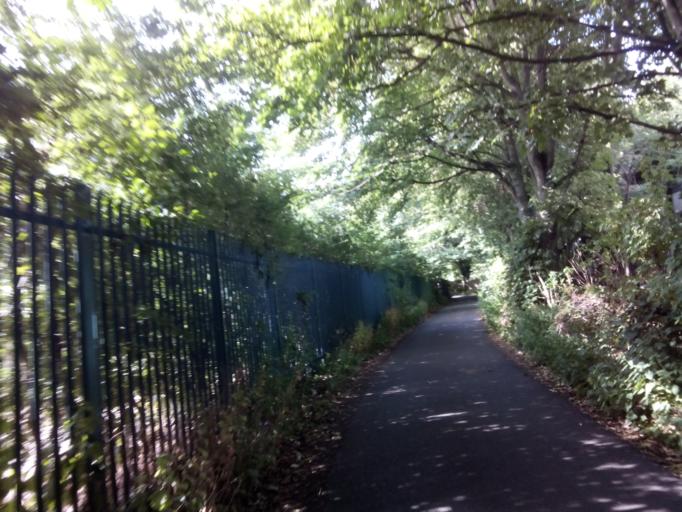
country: GB
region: England
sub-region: County Durham
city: Durham
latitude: 54.7834
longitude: -1.5701
